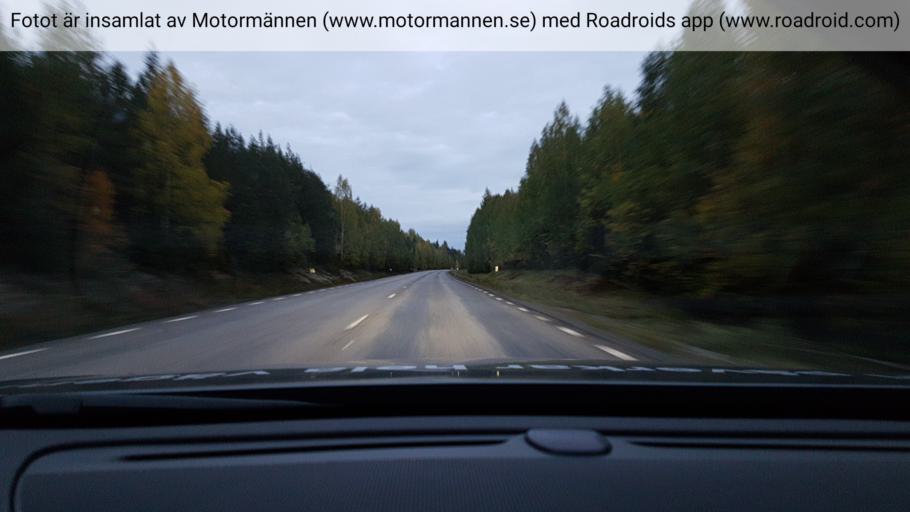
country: SE
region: Norrbotten
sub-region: Alvsbyns Kommun
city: AElvsbyn
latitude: 65.7805
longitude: 20.8218
